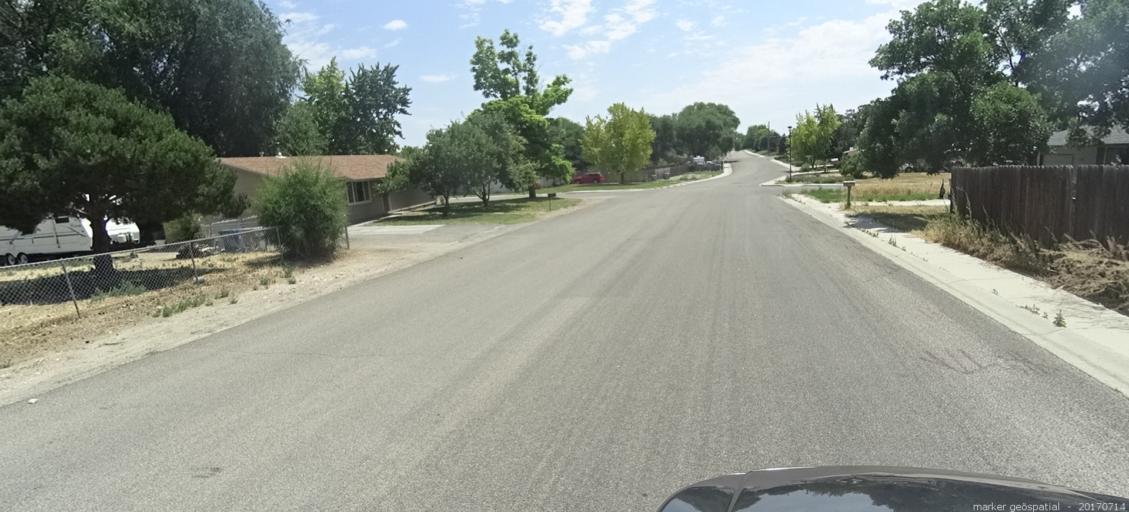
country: US
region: Idaho
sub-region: Ada County
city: Meridian
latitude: 43.5337
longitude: -116.3244
